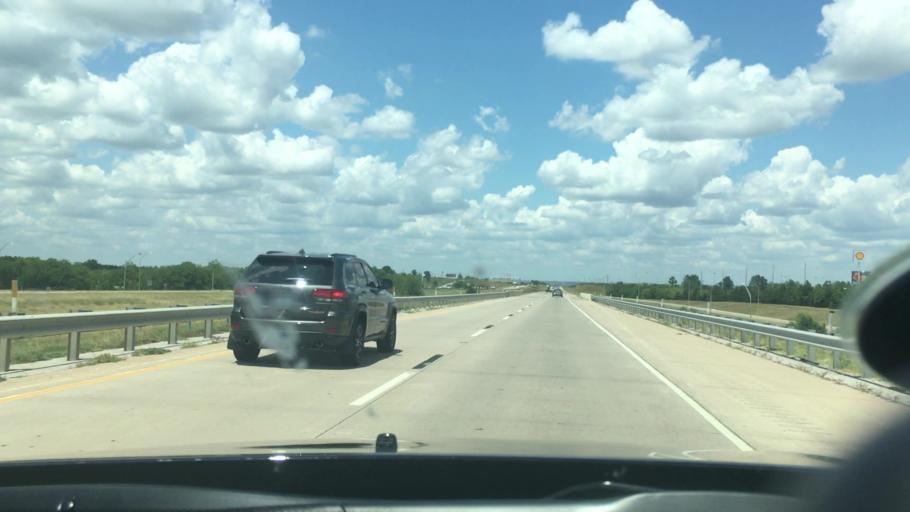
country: US
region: Oklahoma
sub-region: Carter County
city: Ardmore
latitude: 34.2005
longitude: -97.1638
